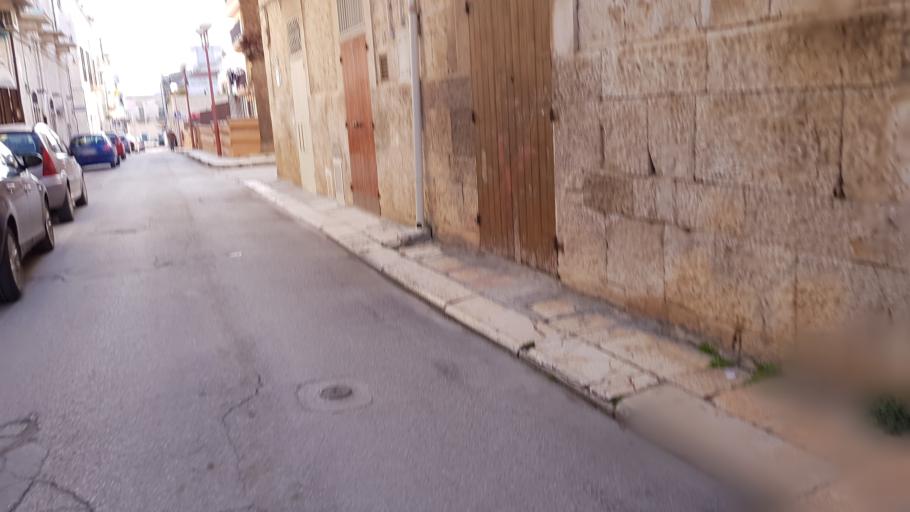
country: IT
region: Apulia
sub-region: Provincia di Bari
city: Ruvo di Puglia
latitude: 41.1193
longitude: 16.4833
